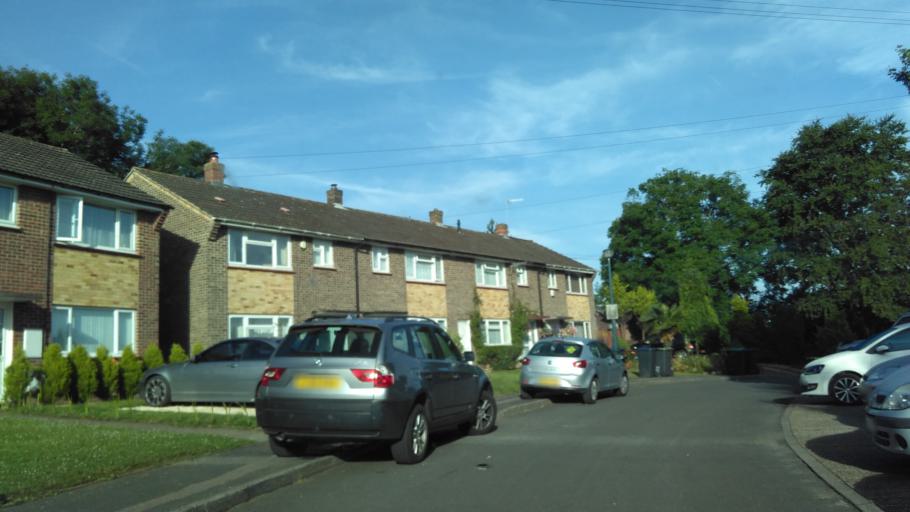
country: GB
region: England
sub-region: Kent
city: Chartham
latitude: 51.2528
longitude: 1.0167
